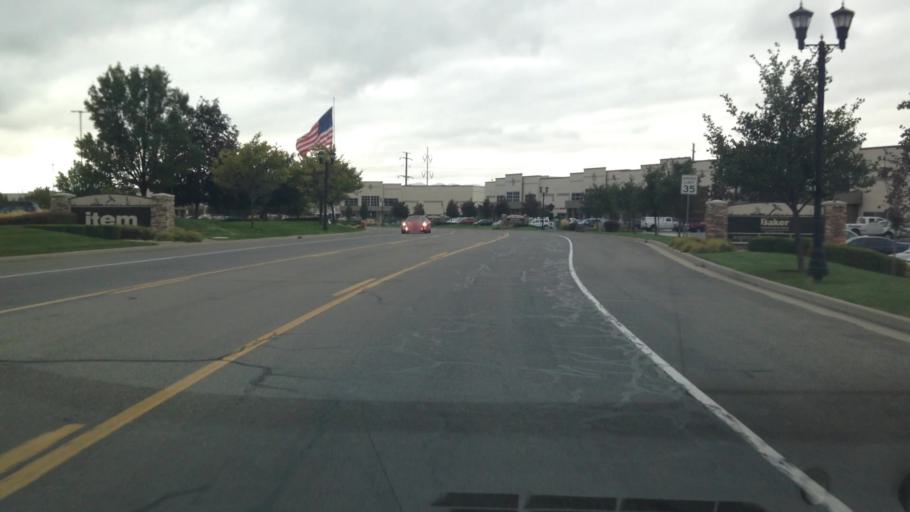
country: US
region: Utah
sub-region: Salt Lake County
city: Sandy City
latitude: 40.5753
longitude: -111.9058
